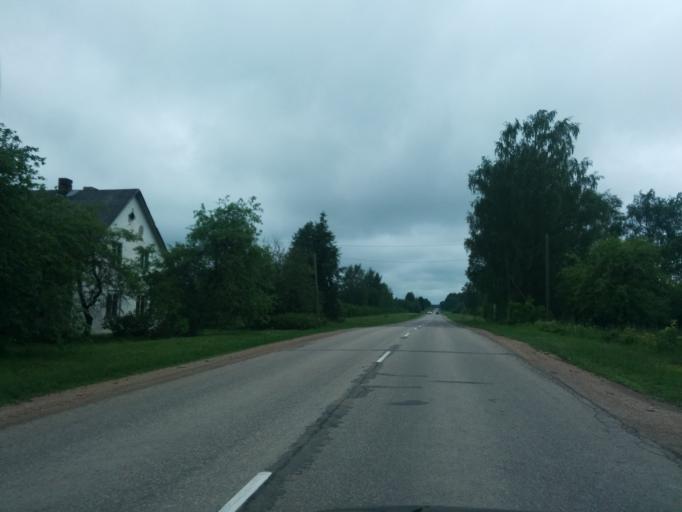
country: LV
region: Balvu Rajons
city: Balvi
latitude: 57.1472
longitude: 27.2333
